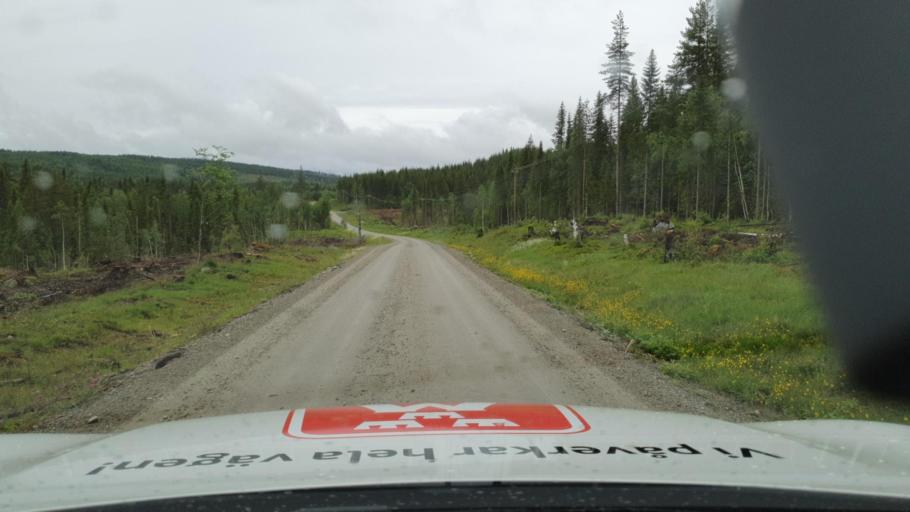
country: SE
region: Vaesterbotten
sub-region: Asele Kommun
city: Asele
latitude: 63.9699
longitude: 16.9176
